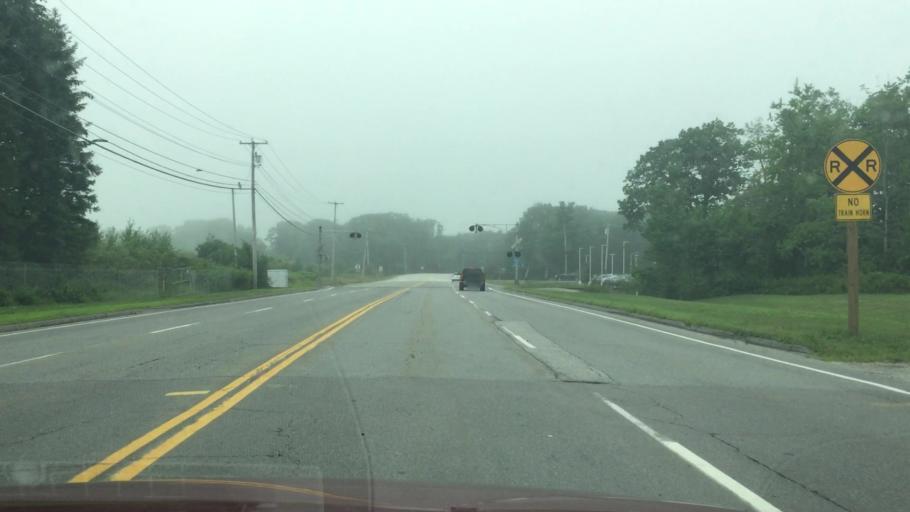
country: US
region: Maine
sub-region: Cumberland County
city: Westbrook
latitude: 43.6745
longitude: -70.3351
